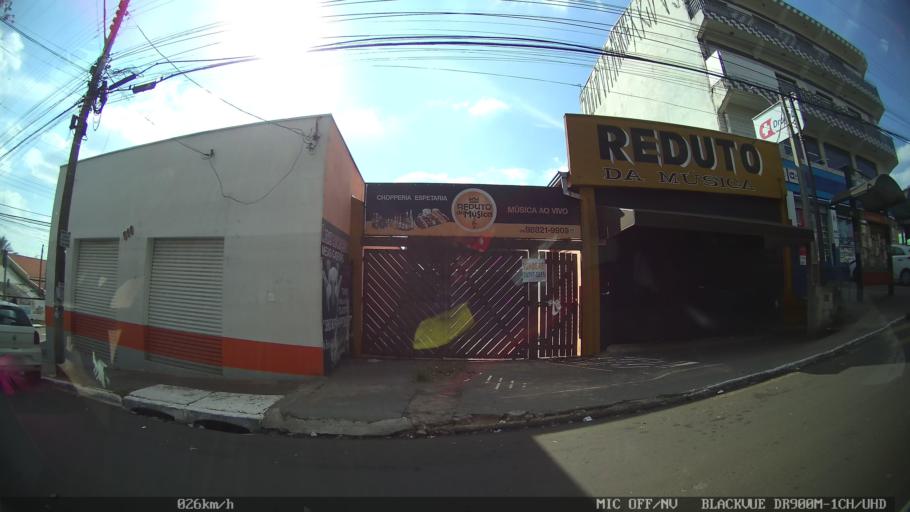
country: BR
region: Sao Paulo
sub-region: Hortolandia
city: Hortolandia
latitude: -22.8996
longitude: -47.2347
